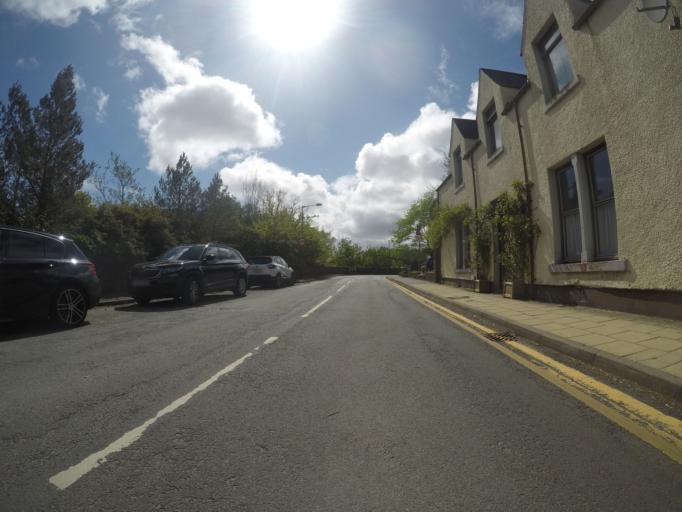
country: GB
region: Scotland
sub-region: Highland
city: Portree
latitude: 57.4135
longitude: -6.1897
